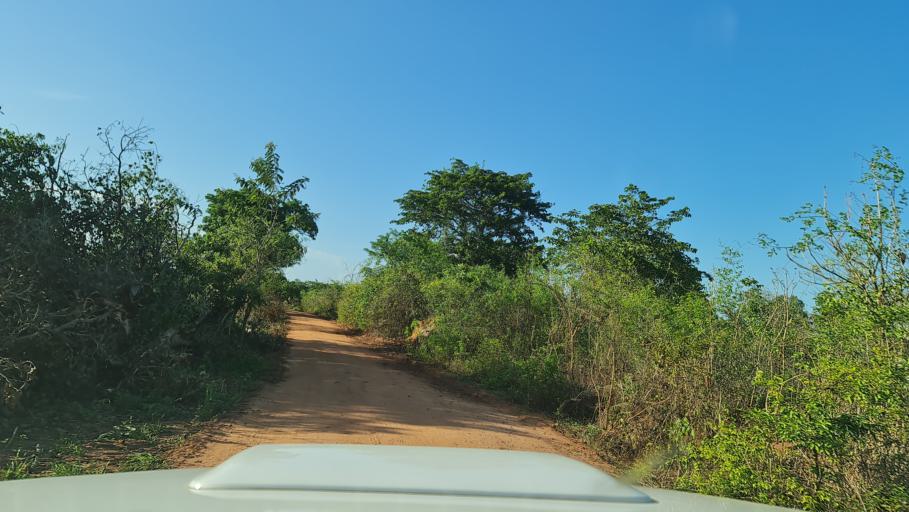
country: MZ
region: Nampula
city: Nacala
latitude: -14.7055
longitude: 40.3325
